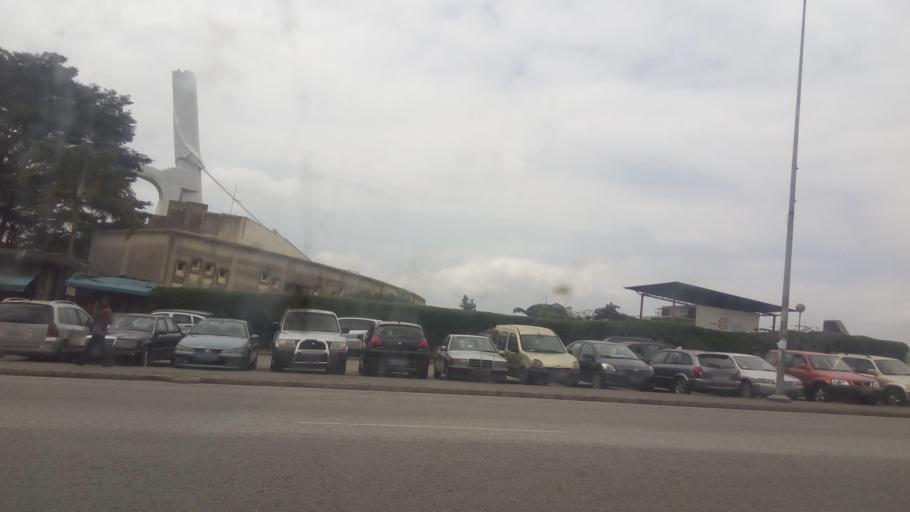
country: CI
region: Lagunes
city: Abidjan
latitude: 5.3333
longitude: -4.0217
